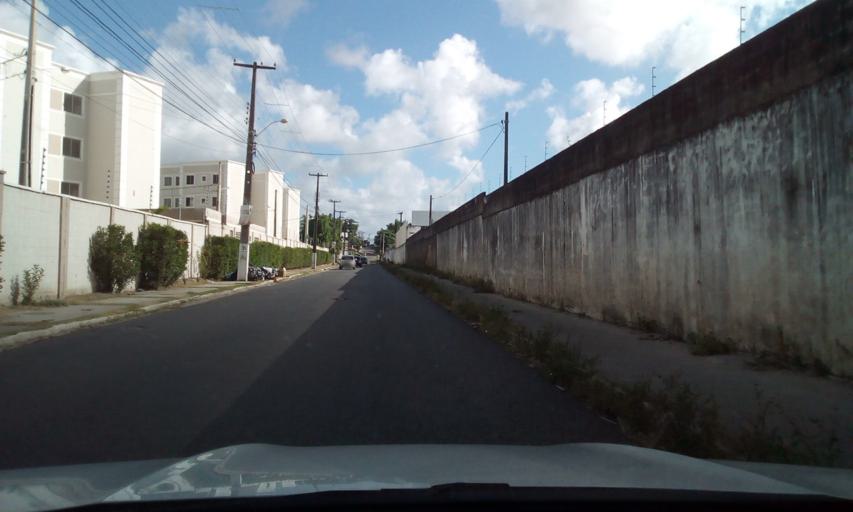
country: BR
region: Paraiba
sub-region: Bayeux
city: Bayeux
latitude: -7.1699
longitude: -34.8960
